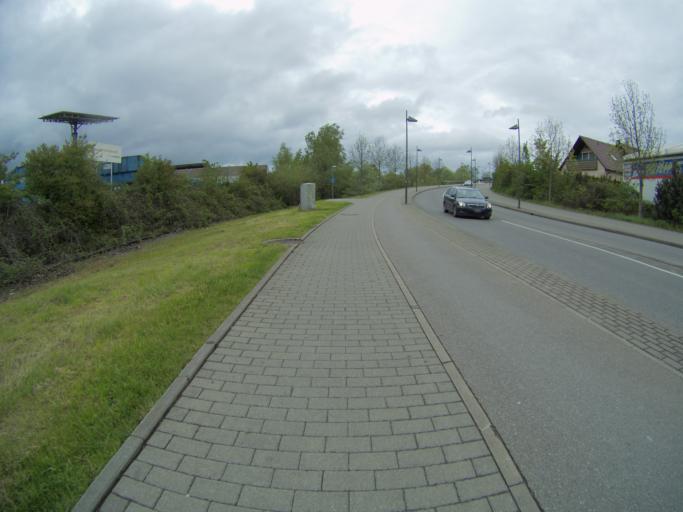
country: DE
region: Baden-Wuerttemberg
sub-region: Freiburg Region
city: Konstanz
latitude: 47.6766
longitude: 9.1603
